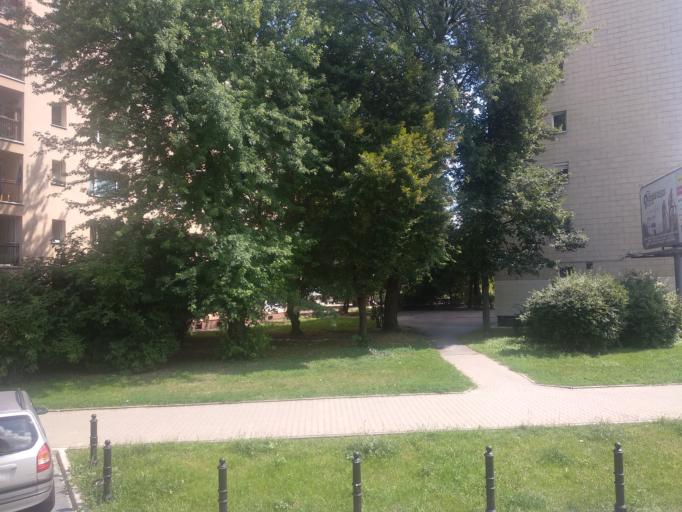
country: PL
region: Masovian Voivodeship
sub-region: Warszawa
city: Wola
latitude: 52.2509
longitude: 20.9939
